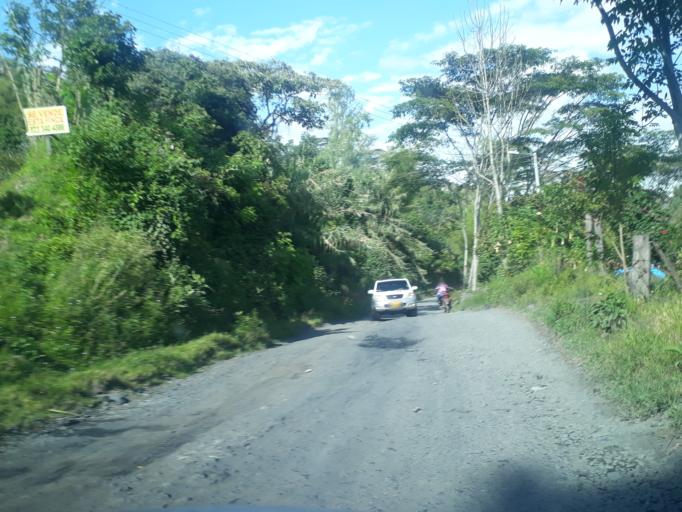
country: CO
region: Santander
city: Velez
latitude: 6.0227
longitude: -73.6593
